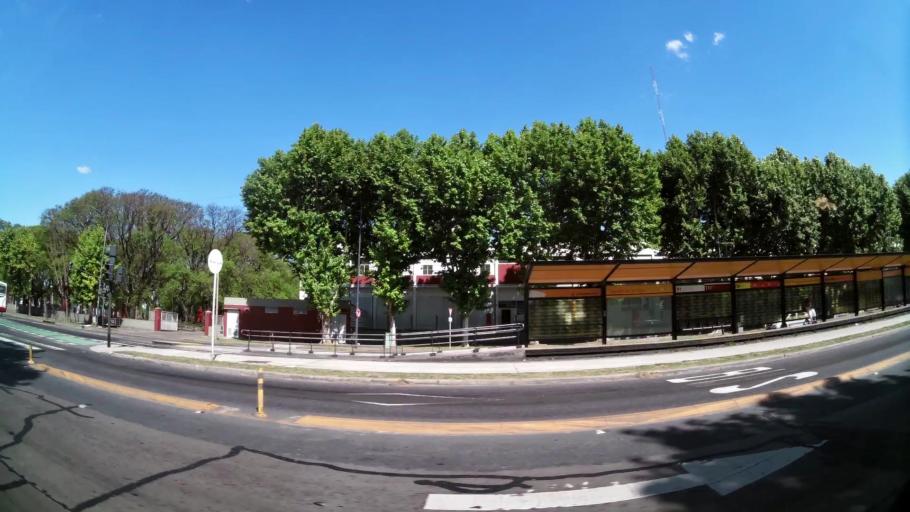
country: AR
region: Buenos Aires F.D.
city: Villa Lugano
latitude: -34.6919
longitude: -58.4637
